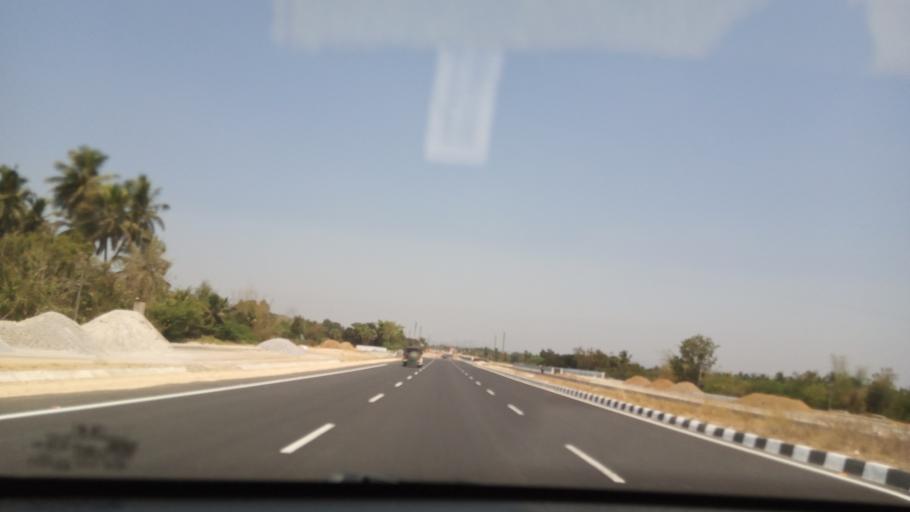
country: IN
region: Andhra Pradesh
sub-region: Chittoor
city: Pakala
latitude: 13.3627
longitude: 79.0881
